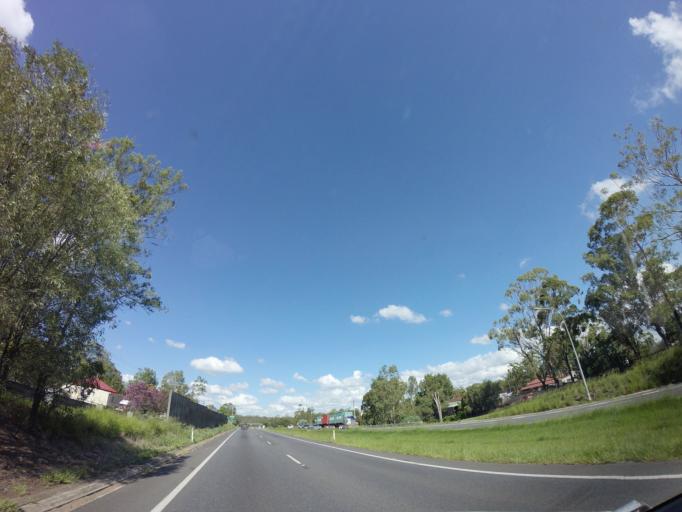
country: AU
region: Queensland
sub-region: Ipswich
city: Tivoli
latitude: -27.5756
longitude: 152.7851
